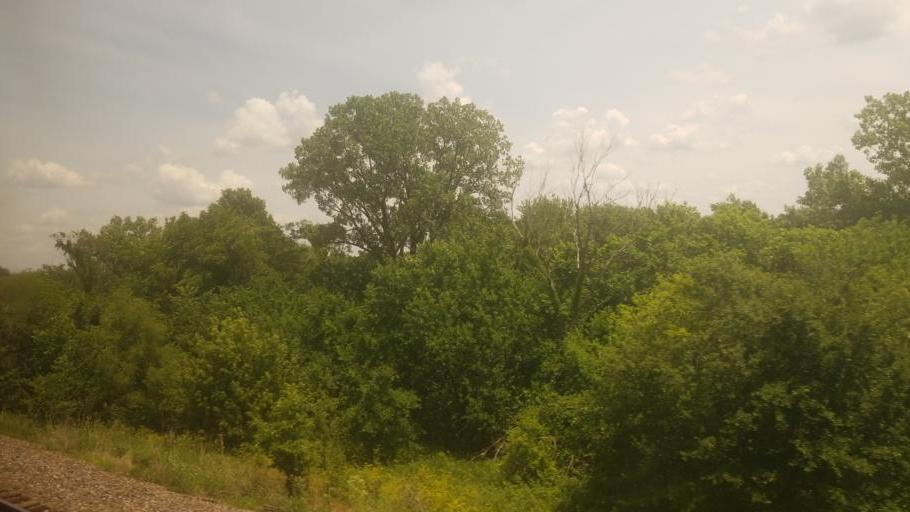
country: US
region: Missouri
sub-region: Macon County
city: La Plata
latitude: 40.0915
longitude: -92.4200
